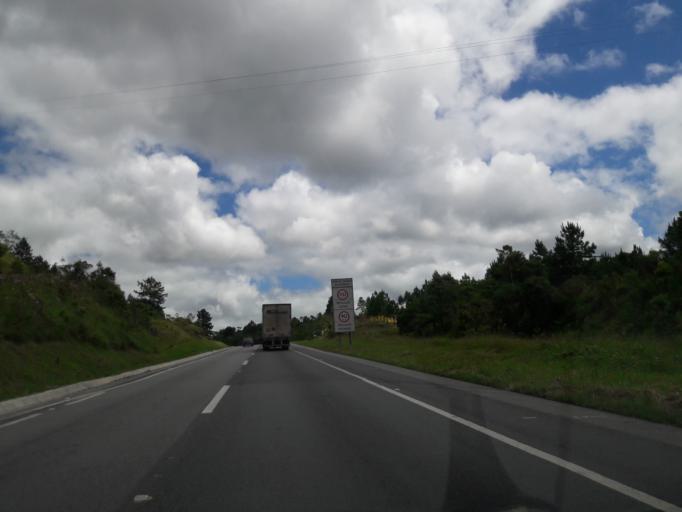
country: BR
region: Parana
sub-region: Antonina
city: Antonina
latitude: -25.1100
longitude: -48.7579
